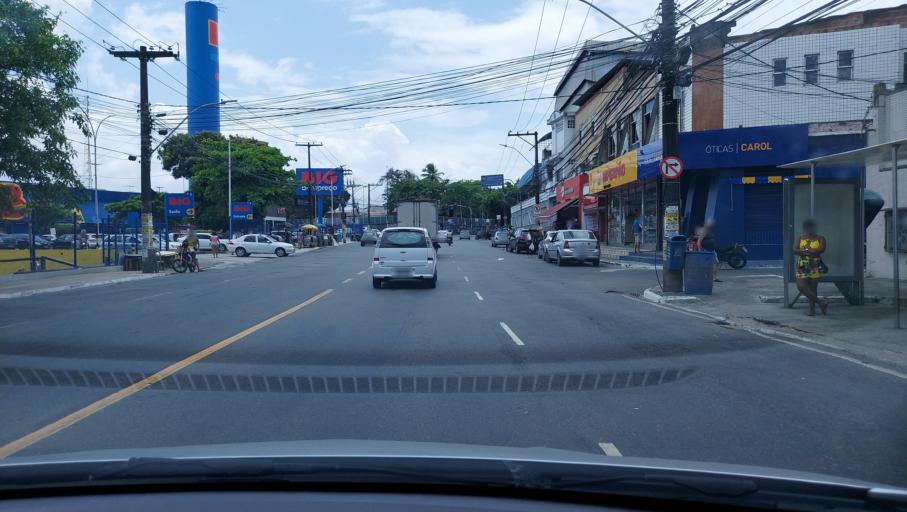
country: BR
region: Bahia
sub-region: Salvador
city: Salvador
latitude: -12.9536
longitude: -38.4615
